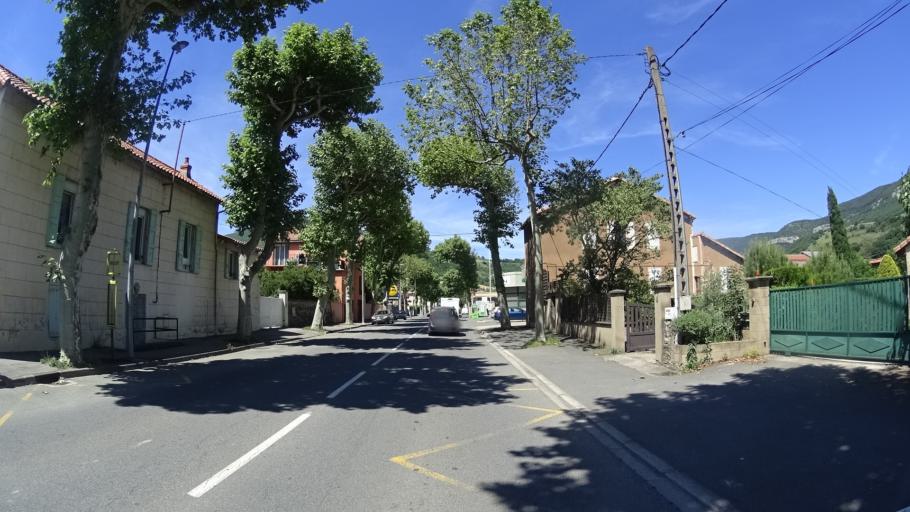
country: FR
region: Midi-Pyrenees
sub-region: Departement de l'Aveyron
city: Millau
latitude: 44.1118
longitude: 3.0823
